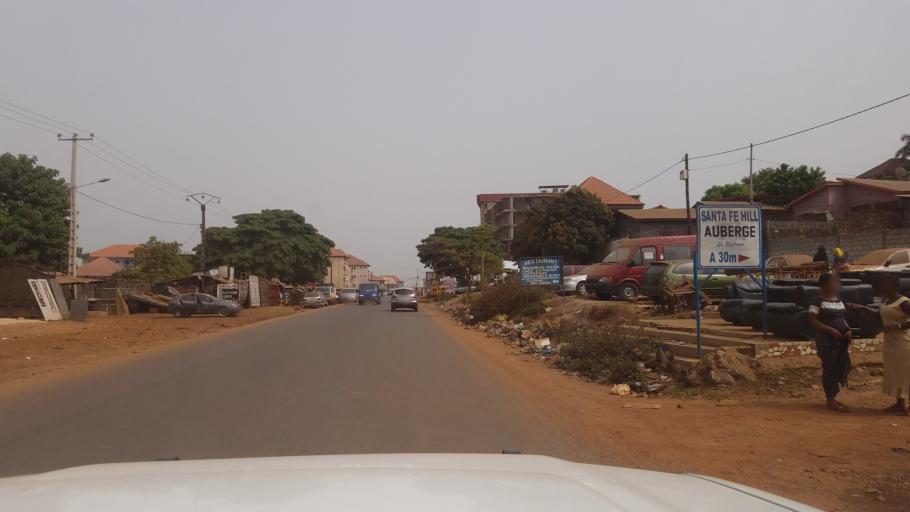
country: GN
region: Conakry
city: Conakry
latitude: 9.6560
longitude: -13.6000
